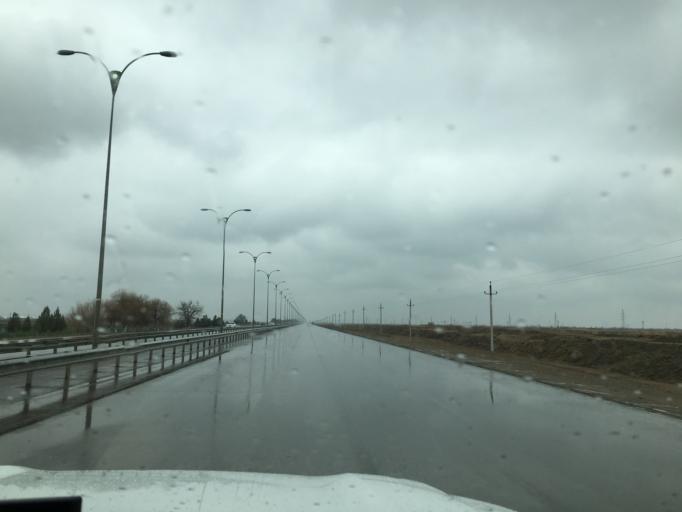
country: TM
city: Murgab
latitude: 37.5101
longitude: 61.9388
